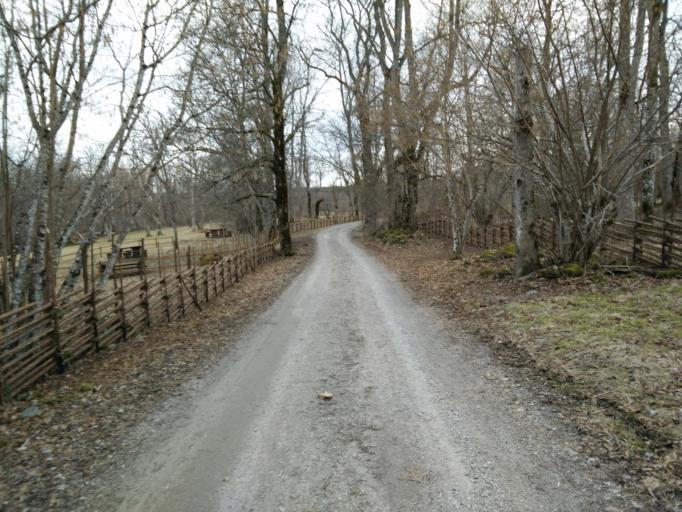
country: SE
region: OErebro
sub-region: Orebro Kommun
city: Garphyttan
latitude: 59.2789
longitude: 14.8875
